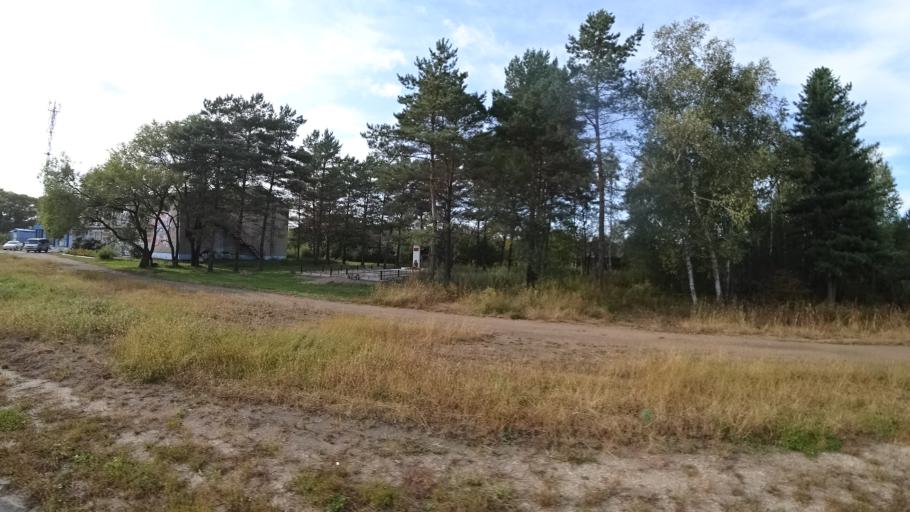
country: RU
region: Amur
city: Arkhara
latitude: 49.3639
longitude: 130.1236
